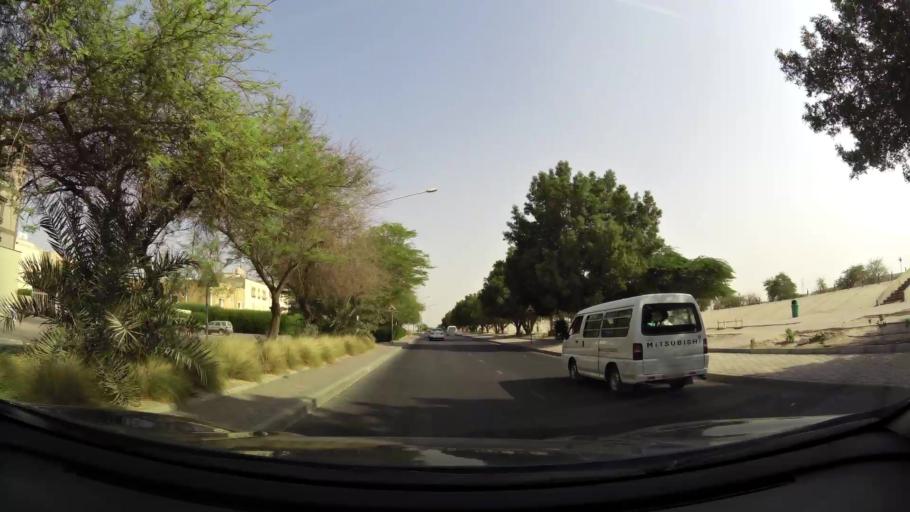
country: KW
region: Muhafazat al Jahra'
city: Al Jahra'
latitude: 29.3175
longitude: 47.6727
